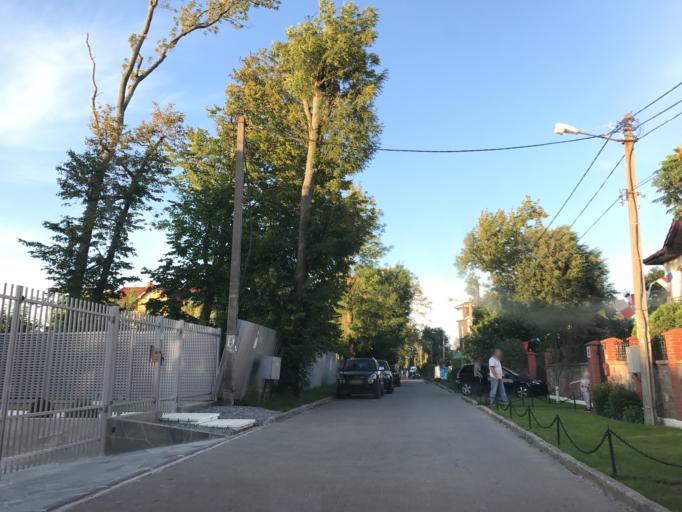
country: RU
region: Kaliningrad
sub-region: Zelenogradskiy Rayon
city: Zelenogradsk
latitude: 54.9574
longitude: 20.4631
